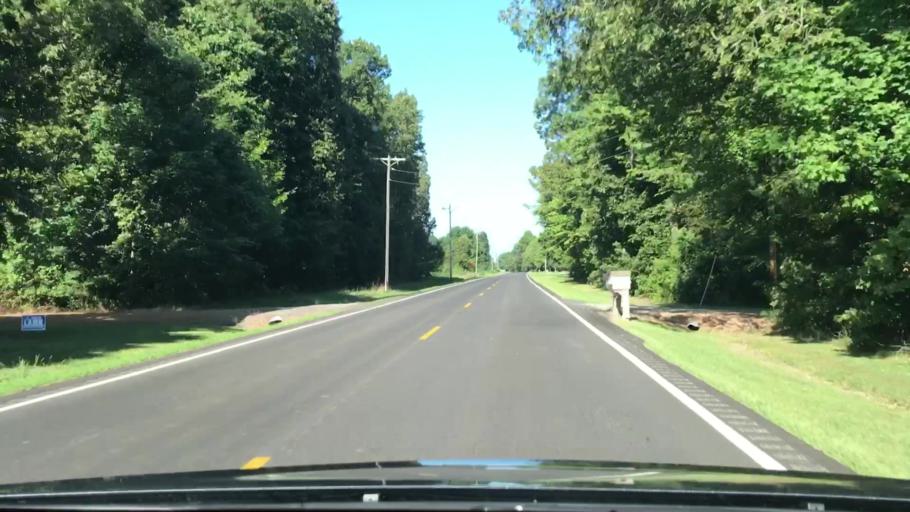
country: US
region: Kentucky
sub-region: Marshall County
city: Benton
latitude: 36.7650
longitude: -88.3852
